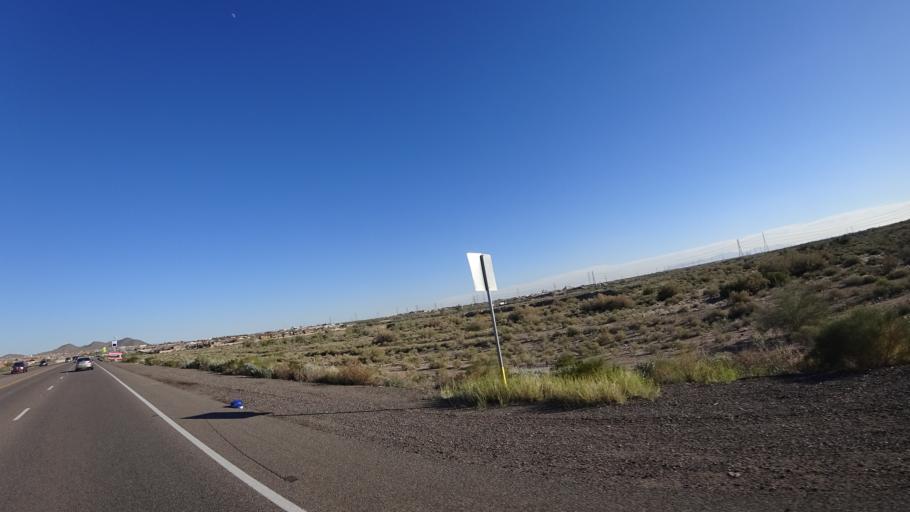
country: US
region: Arizona
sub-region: Maricopa County
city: Sun City West
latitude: 33.7136
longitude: -112.2992
